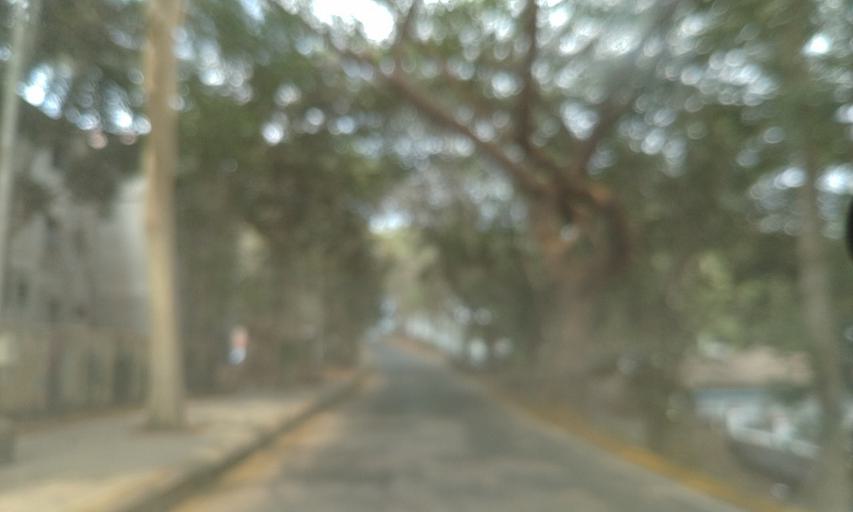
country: IN
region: Goa
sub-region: North Goa
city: Panaji
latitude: 15.4888
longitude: 73.8284
